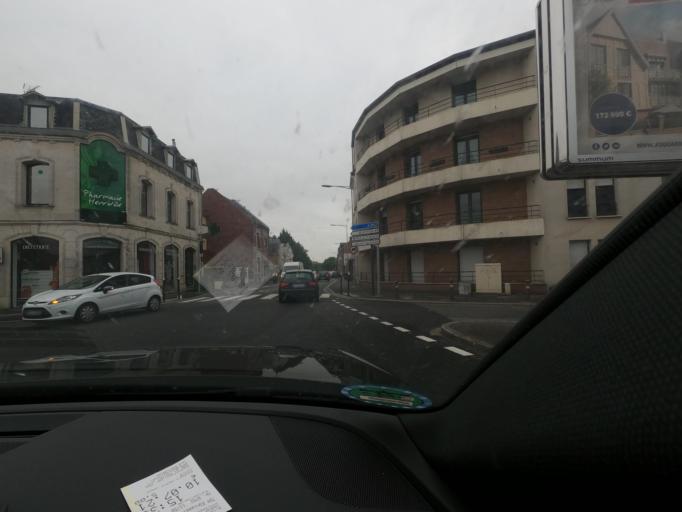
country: FR
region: Picardie
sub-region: Departement de la Somme
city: Amiens
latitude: 49.8788
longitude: 2.3051
